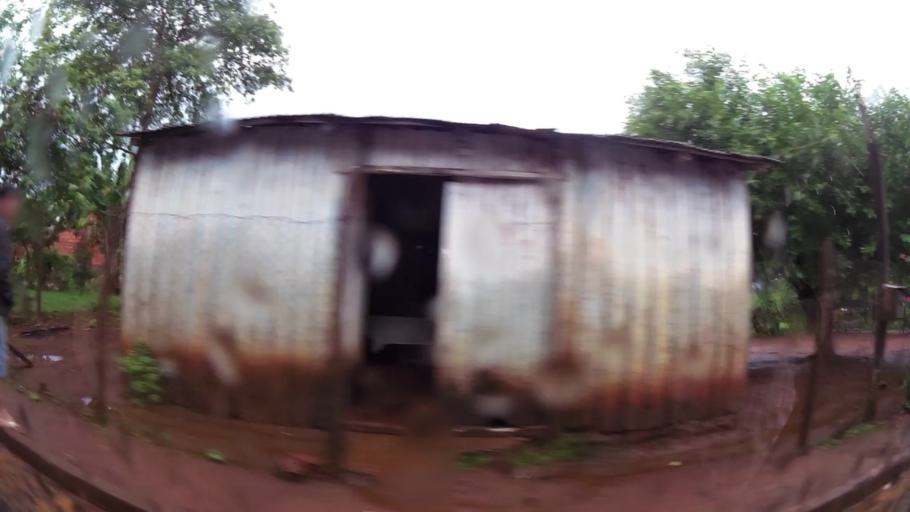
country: PY
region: Alto Parana
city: Presidente Franco
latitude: -25.5559
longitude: -54.6509
